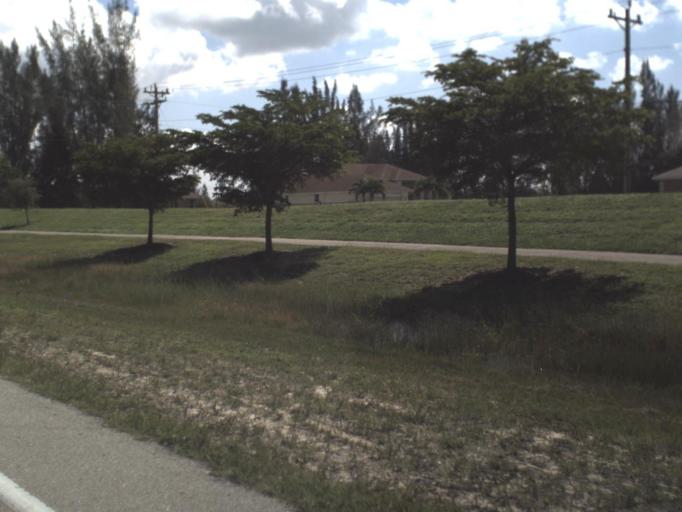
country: US
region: Florida
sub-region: Lee County
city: Cape Coral
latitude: 26.6069
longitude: -82.0113
